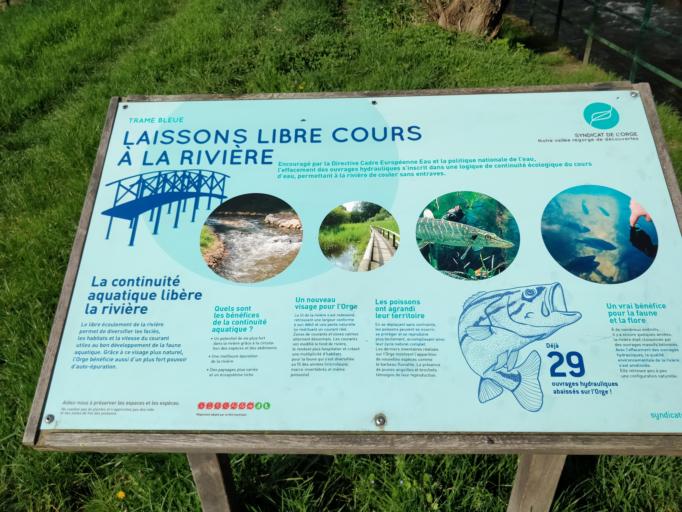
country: FR
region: Ile-de-France
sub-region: Departement de l'Essonne
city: Epinay-sur-Orge
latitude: 48.6637
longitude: 2.3163
